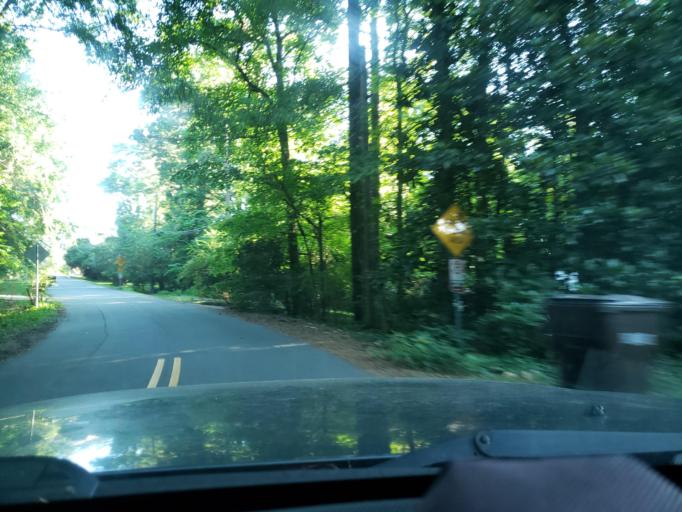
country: US
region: North Carolina
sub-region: Orange County
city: Chapel Hill
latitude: 35.8966
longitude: -79.0457
